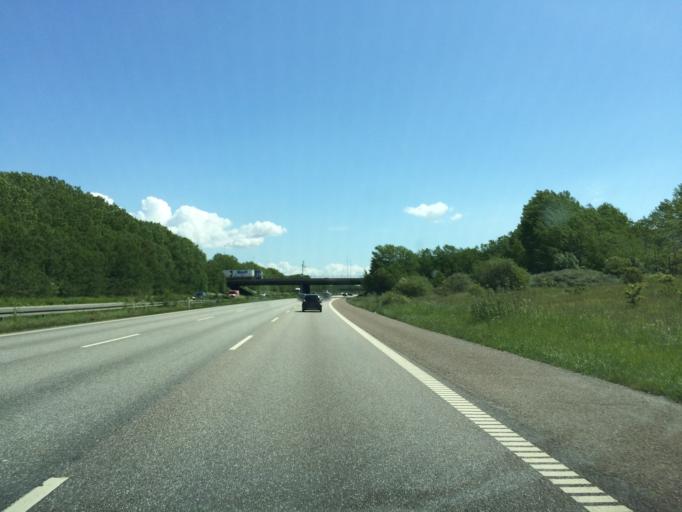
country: DK
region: Capital Region
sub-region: Hvidovre Kommune
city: Hvidovre
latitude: 55.6163
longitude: 12.4721
